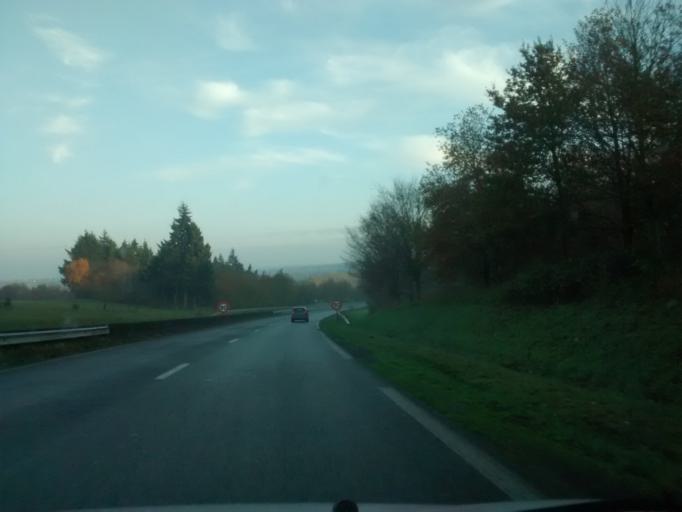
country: FR
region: Brittany
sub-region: Departement d'Ille-et-Vilaine
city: Sens-de-Bretagne
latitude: 48.3606
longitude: -1.5083
